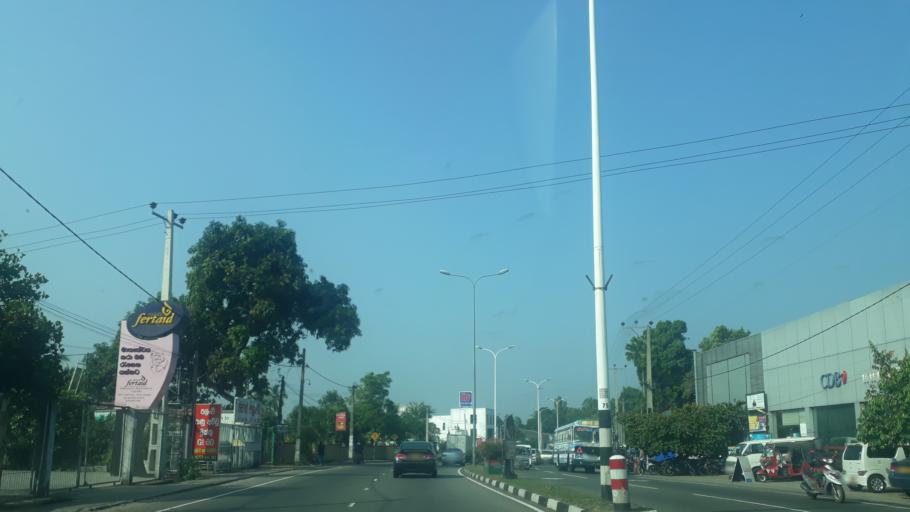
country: LK
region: Western
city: Kelaniya
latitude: 6.9935
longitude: 79.9439
